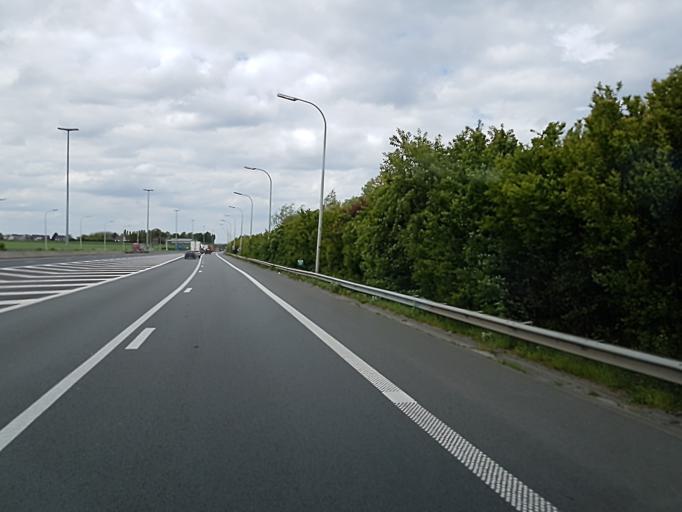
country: BE
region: Wallonia
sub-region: Province du Hainaut
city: Mouscron
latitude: 50.7934
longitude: 3.2238
